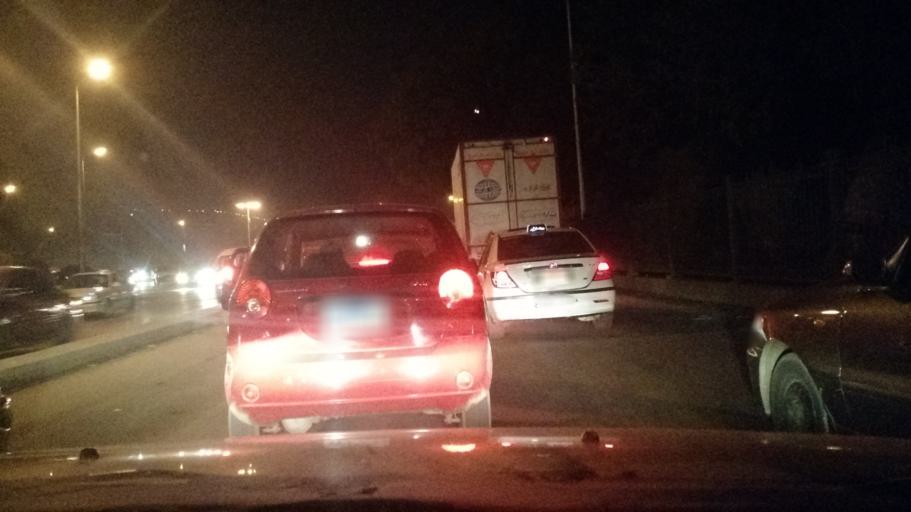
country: EG
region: Al Jizah
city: Al Jizah
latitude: 30.0184
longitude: 31.2506
